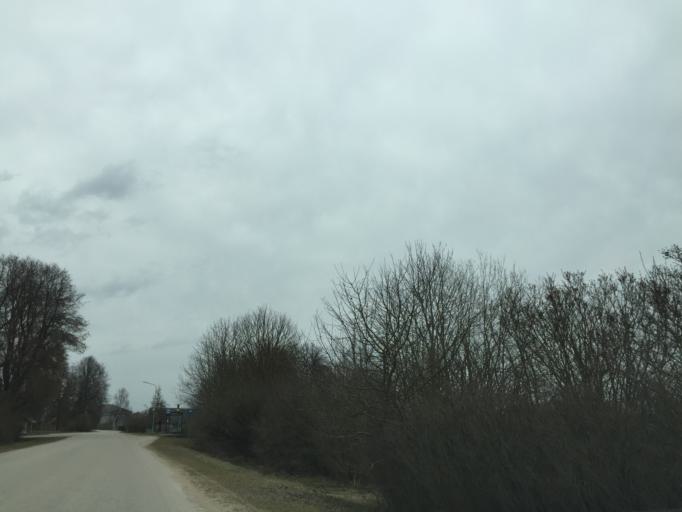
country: LV
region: Livani
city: Livani
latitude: 56.3335
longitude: 26.1606
